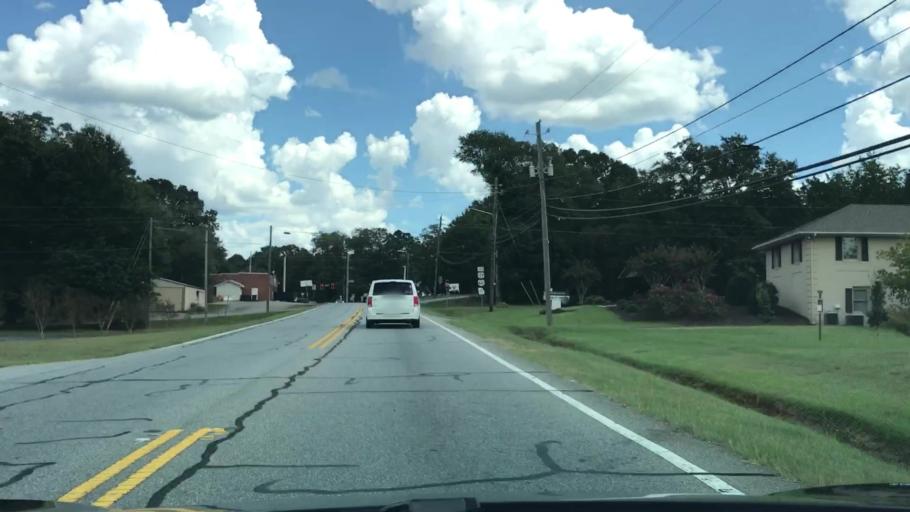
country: US
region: Georgia
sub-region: Oconee County
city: Watkinsville
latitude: 33.8661
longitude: -83.4131
